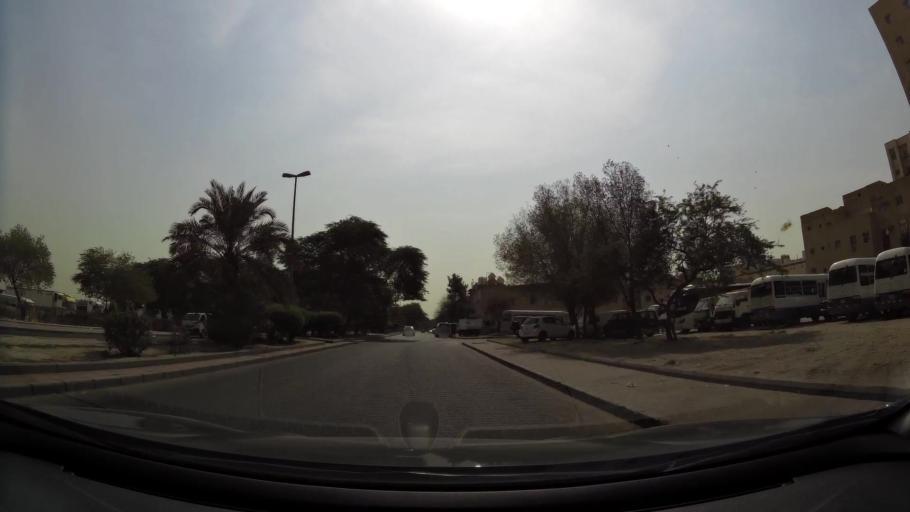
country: KW
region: Al Farwaniyah
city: Al Farwaniyah
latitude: 29.2558
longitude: 47.9454
